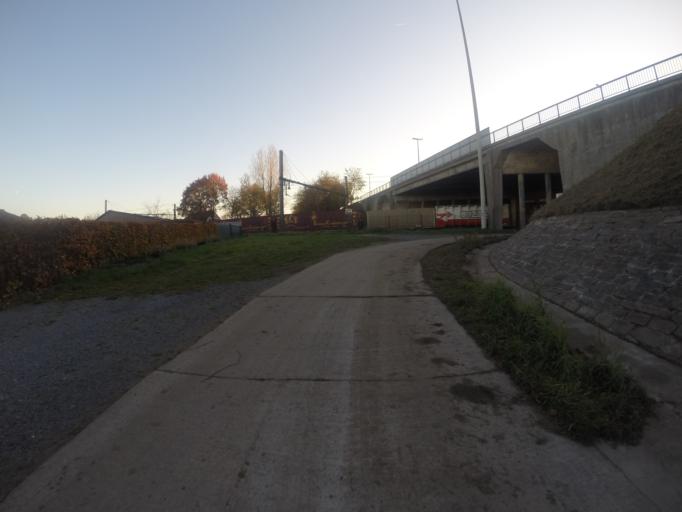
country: BE
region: Flanders
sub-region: Provincie Oost-Vlaanderen
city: Aalter
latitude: 51.0944
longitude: 3.4397
